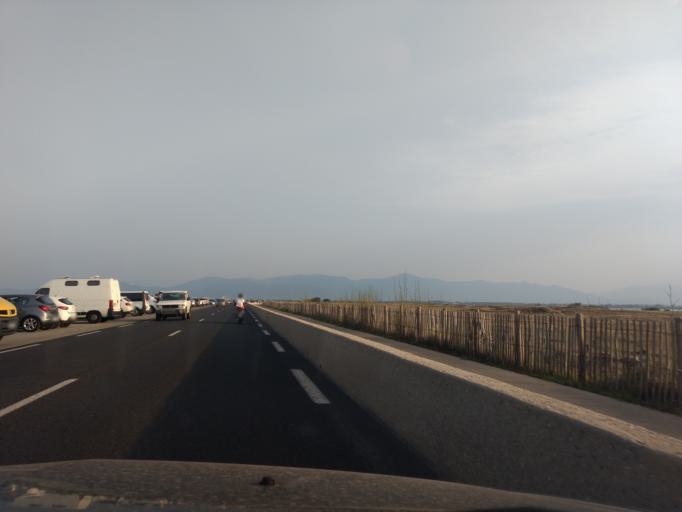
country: FR
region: Languedoc-Roussillon
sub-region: Departement des Pyrenees-Orientales
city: Saint-Cyprien-Plage
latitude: 42.6672
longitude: 3.0330
